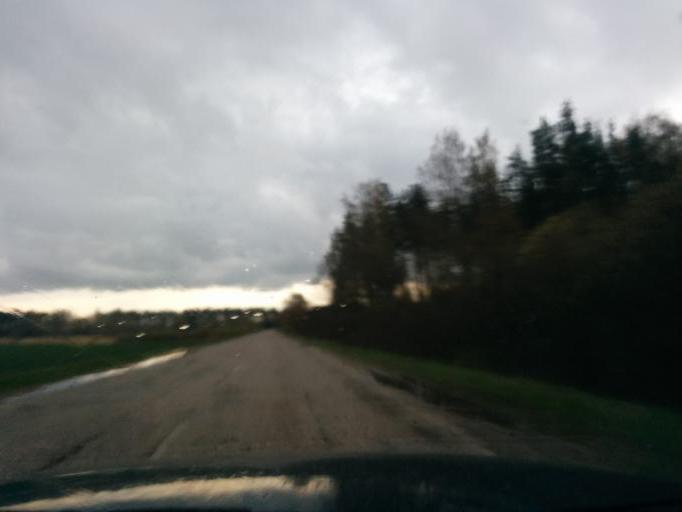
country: LT
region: Siauliu apskritis
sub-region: Joniskis
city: Joniskis
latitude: 56.4168
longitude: 23.6467
